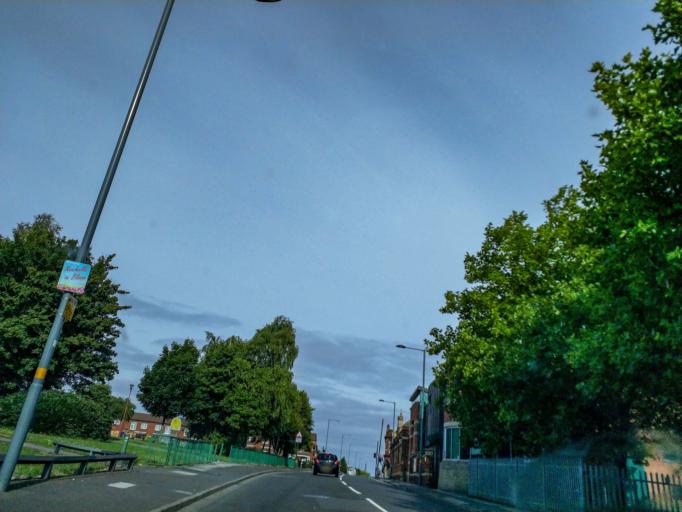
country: GB
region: England
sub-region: City and Borough of Birmingham
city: Birmingham
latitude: 52.5002
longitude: -1.8641
